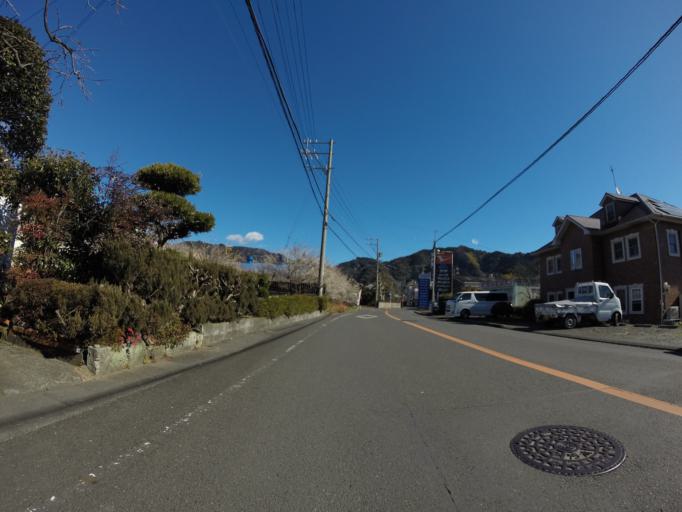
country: JP
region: Shizuoka
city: Shizuoka-shi
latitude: 35.0328
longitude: 138.3932
